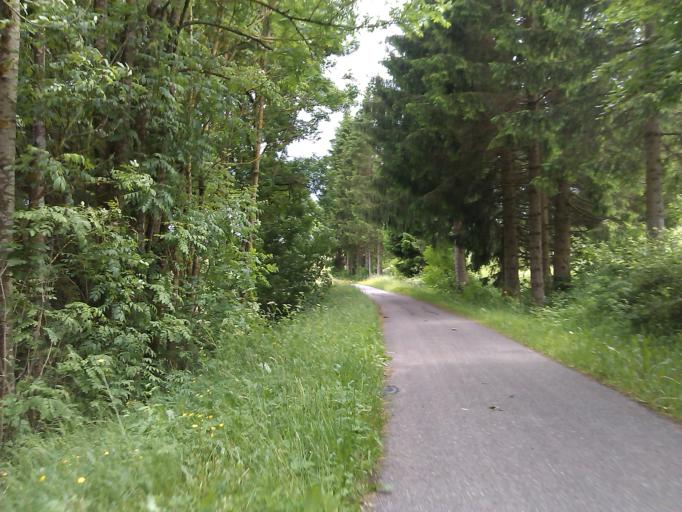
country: DE
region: Bavaria
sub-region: Swabia
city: Rosshaupten
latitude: 47.6879
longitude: 10.7072
